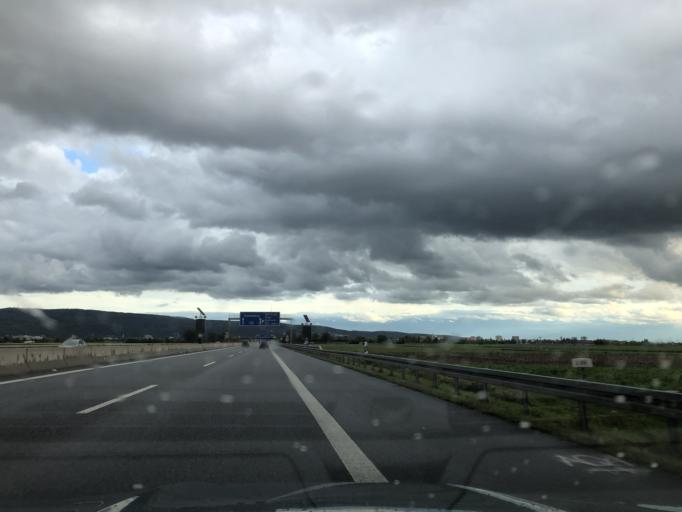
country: DE
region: Baden-Wuerttemberg
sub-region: Karlsruhe Region
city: Edingen-Neckarhausen
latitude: 49.4289
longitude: 8.6148
